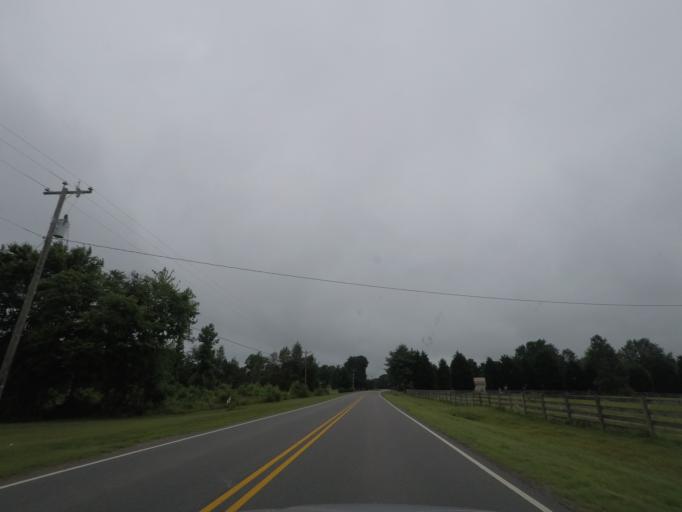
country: US
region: Virginia
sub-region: Fluvanna County
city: Weber City
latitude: 37.6383
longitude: -78.3603
